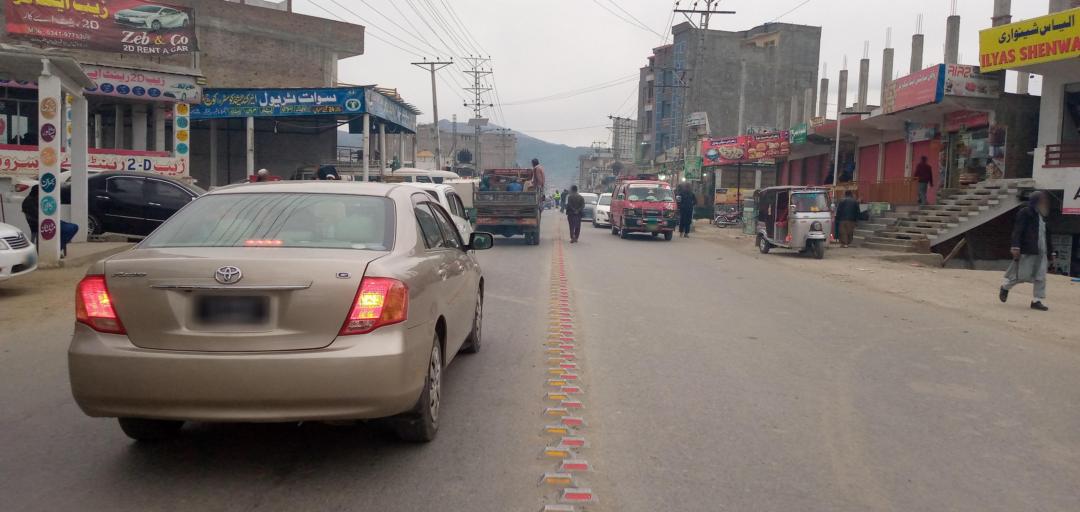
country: PK
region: Khyber Pakhtunkhwa
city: Mingora
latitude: 34.7768
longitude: 72.3332
